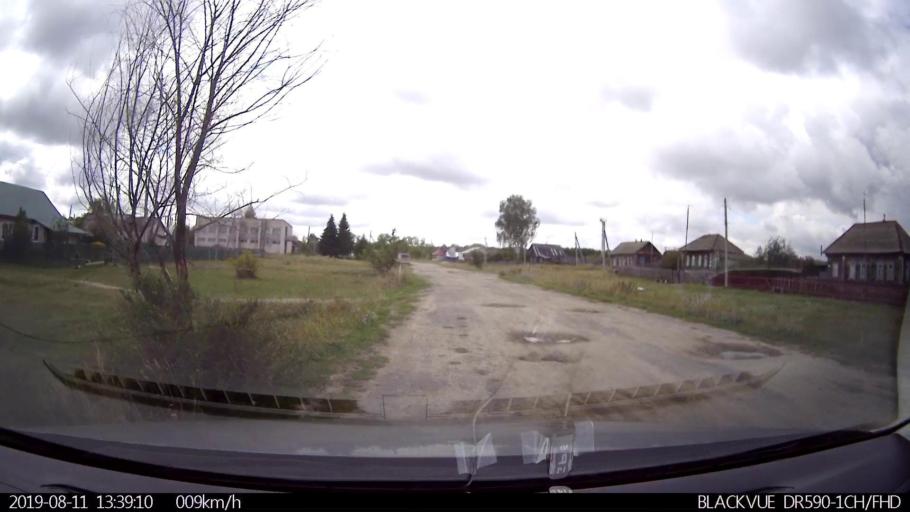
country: RU
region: Ulyanovsk
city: Ignatovka
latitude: 53.8595
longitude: 47.5793
